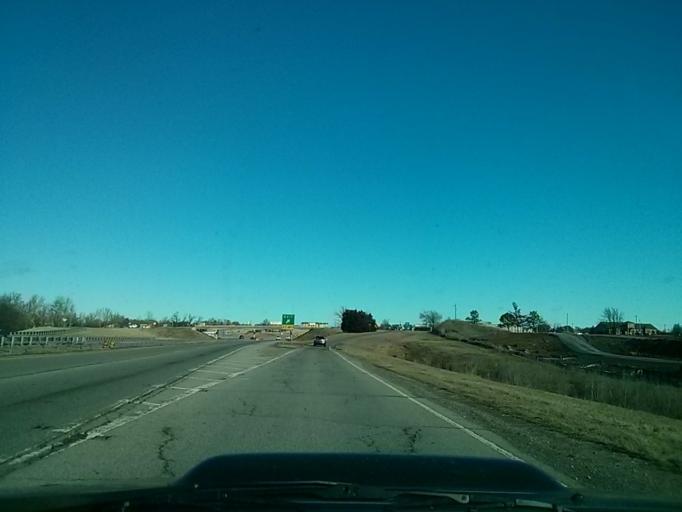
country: US
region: Oklahoma
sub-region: Tulsa County
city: Jenks
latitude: 36.0220
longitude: -96.0115
